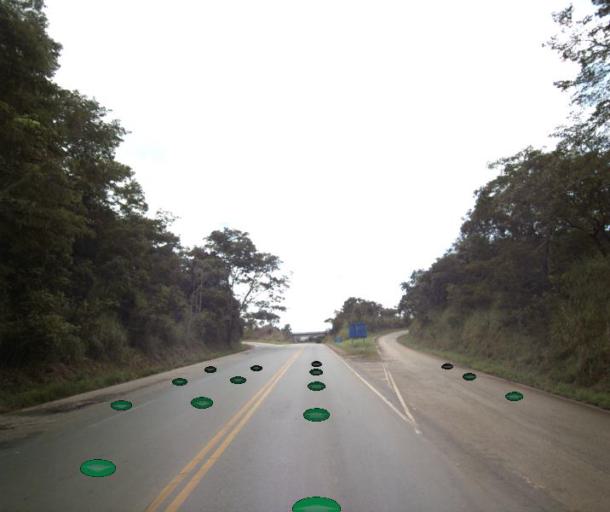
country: BR
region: Goias
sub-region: Jaragua
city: Jaragua
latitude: -15.8945
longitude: -49.2389
